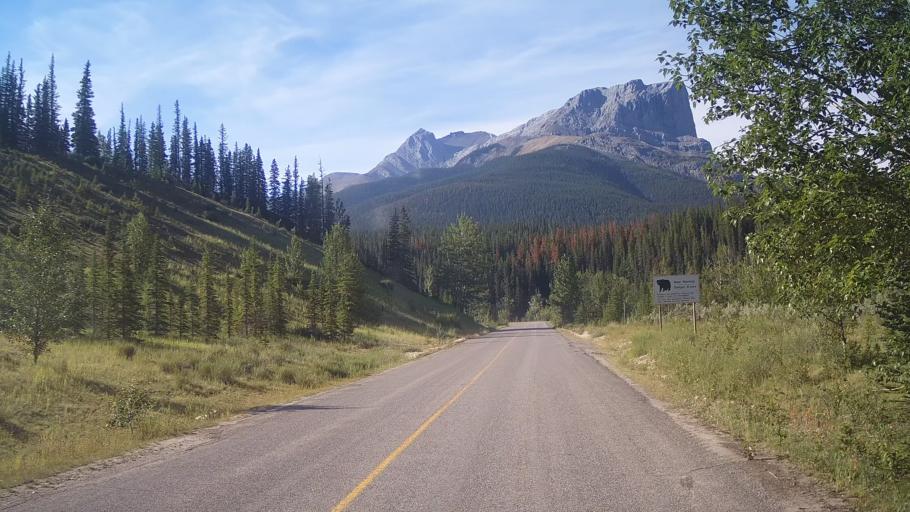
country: CA
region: Alberta
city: Jasper Park Lodge
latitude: 53.2016
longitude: -117.9228
